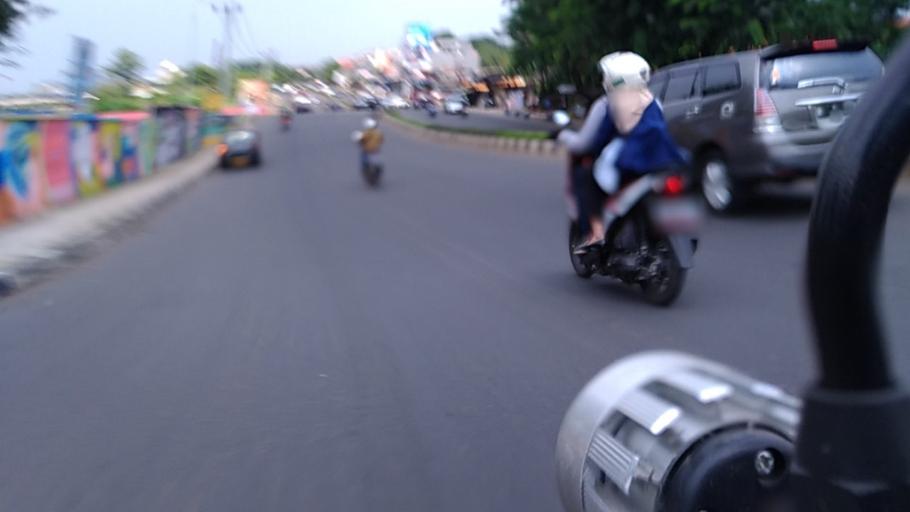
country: ID
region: West Java
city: Depok
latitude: -6.3783
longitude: 106.8359
